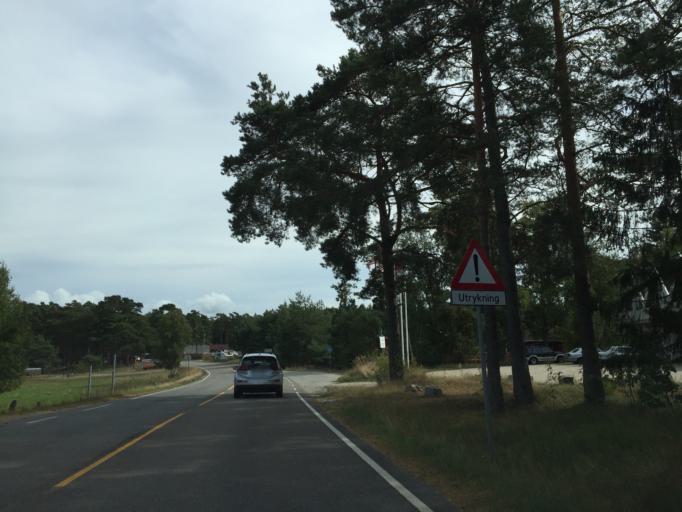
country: NO
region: Ostfold
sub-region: Hvaler
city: Skjaerhalden
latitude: 59.0351
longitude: 11.0158
